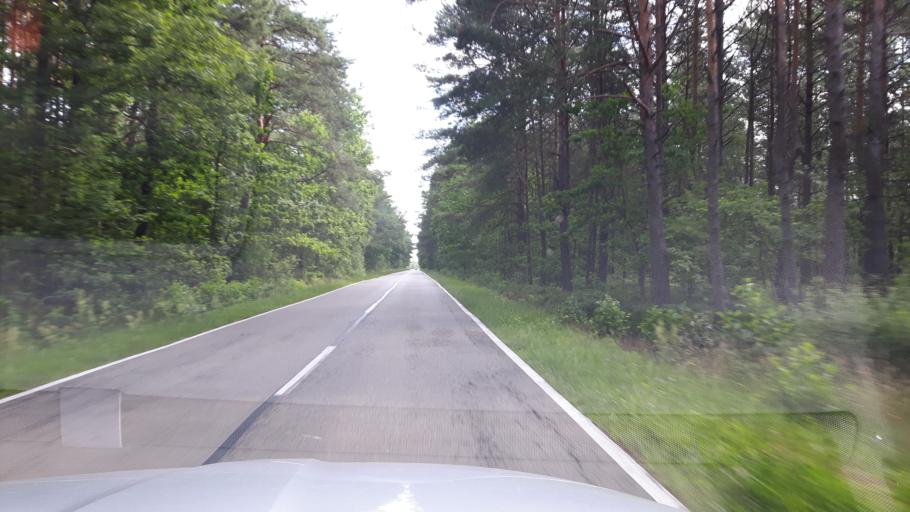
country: PL
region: Masovian Voivodeship
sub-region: Powiat wolominski
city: Strachowka
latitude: 52.4312
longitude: 21.5411
